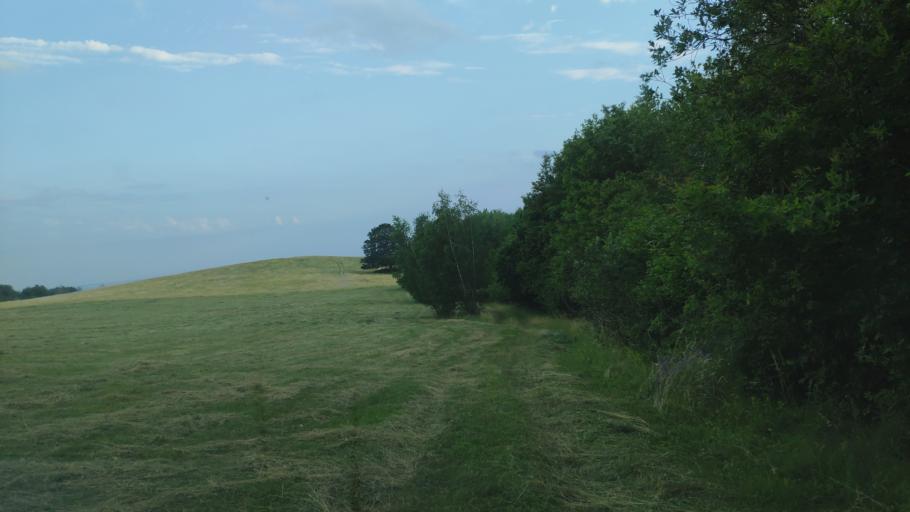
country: SK
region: Kosicky
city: Moldava nad Bodvou
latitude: 48.7169
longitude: 21.0016
